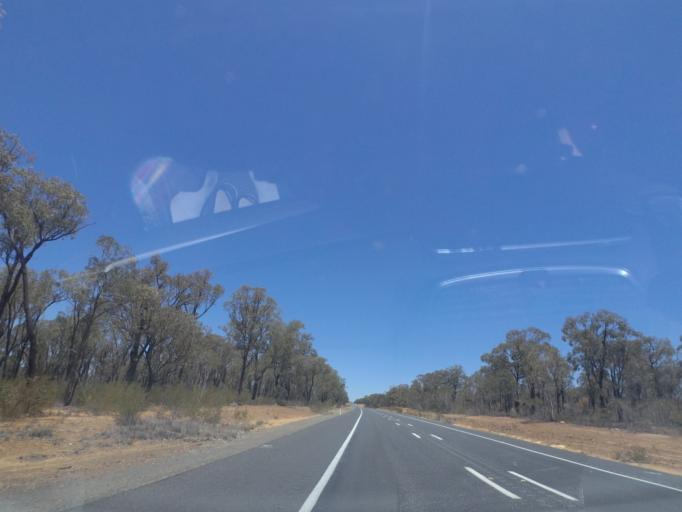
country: AU
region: New South Wales
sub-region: Warrumbungle Shire
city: Coonabarabran
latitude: -30.8887
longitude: 149.4432
